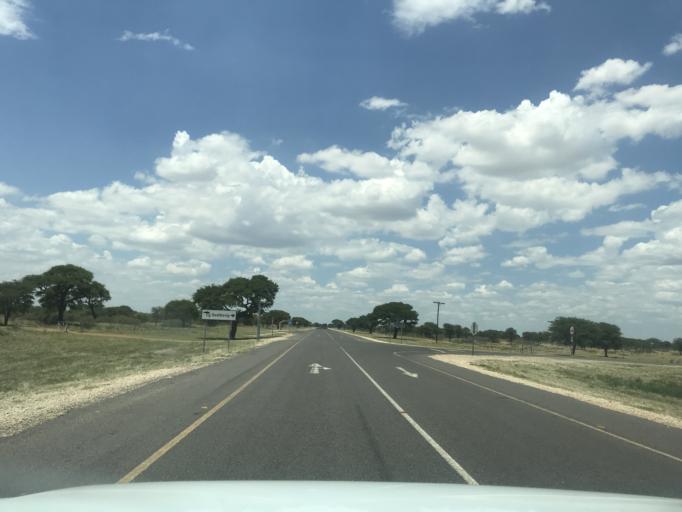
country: BW
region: South East
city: Janeng
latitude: -25.6404
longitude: 25.1511
